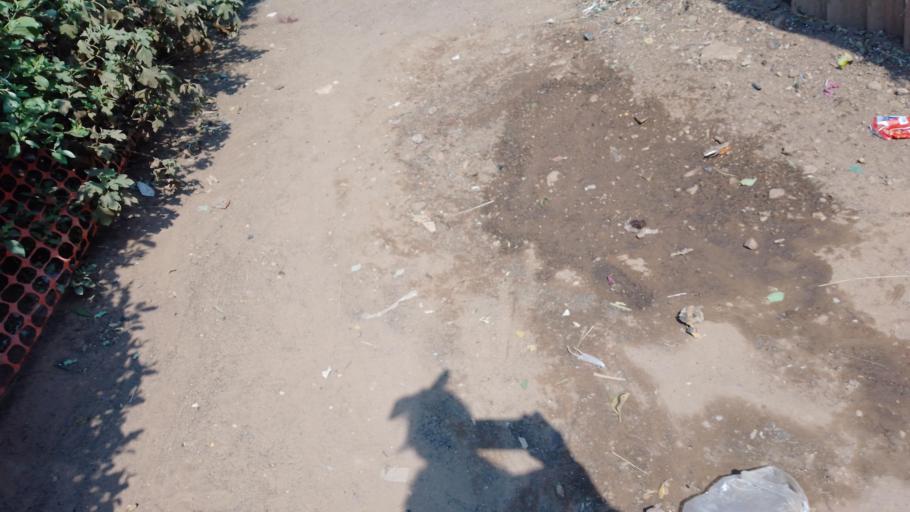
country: ZM
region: Lusaka
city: Lusaka
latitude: -15.3963
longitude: 28.3716
